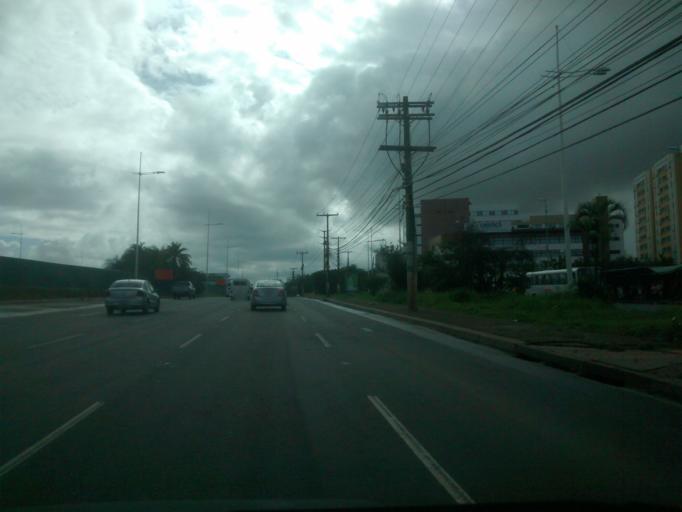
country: BR
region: Bahia
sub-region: Salvador
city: Salvador
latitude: -12.9626
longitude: -38.4340
